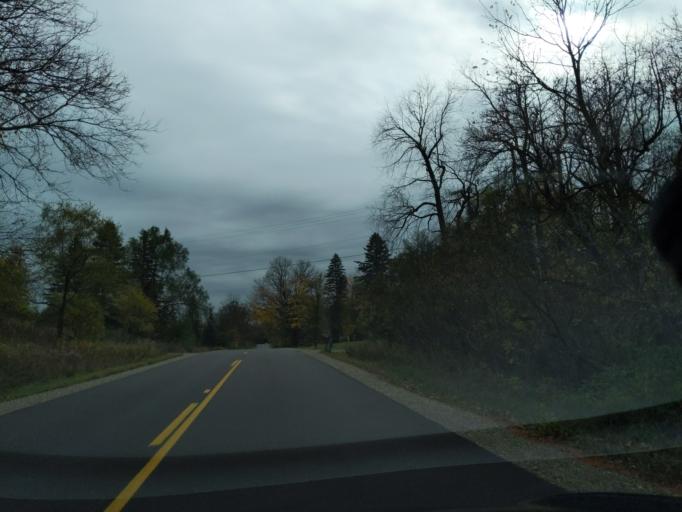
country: US
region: Michigan
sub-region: Eaton County
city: Eaton Rapids
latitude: 42.5281
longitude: -84.6212
